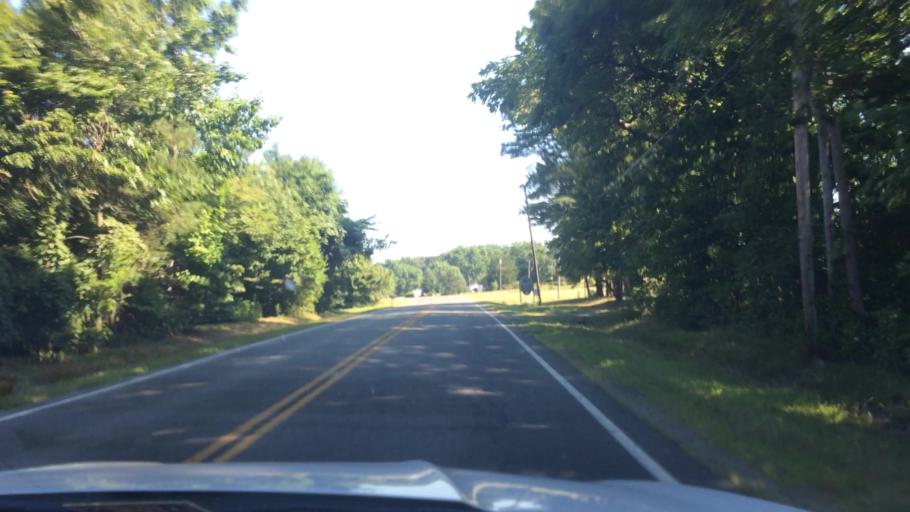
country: US
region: Virginia
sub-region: Lancaster County
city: Lancaster
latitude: 37.8360
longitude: -76.5774
